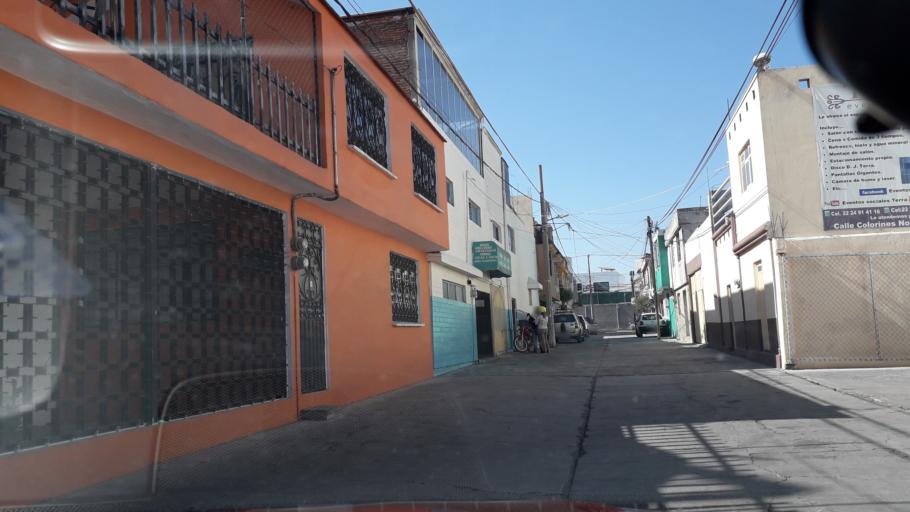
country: MX
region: Puebla
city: Puebla
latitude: 19.0775
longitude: -98.2136
